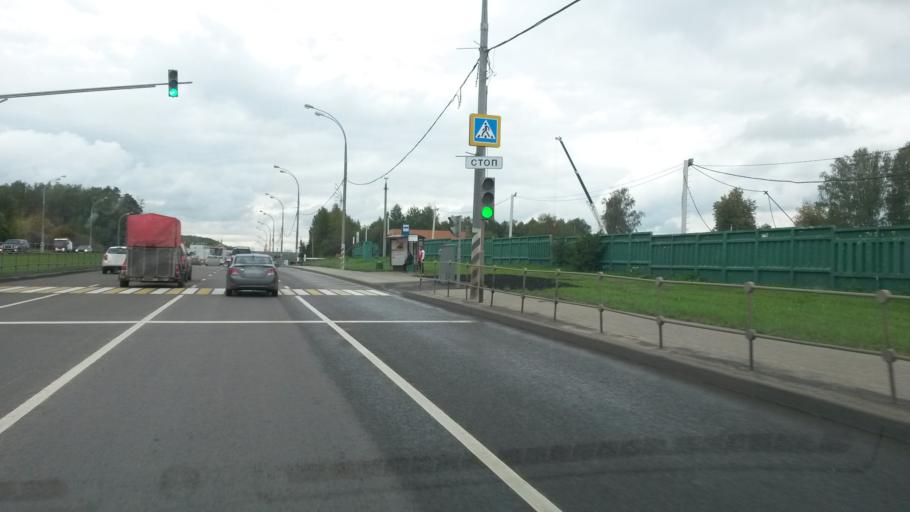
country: RU
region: Moscow
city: Annino
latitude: 55.5579
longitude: 37.5542
